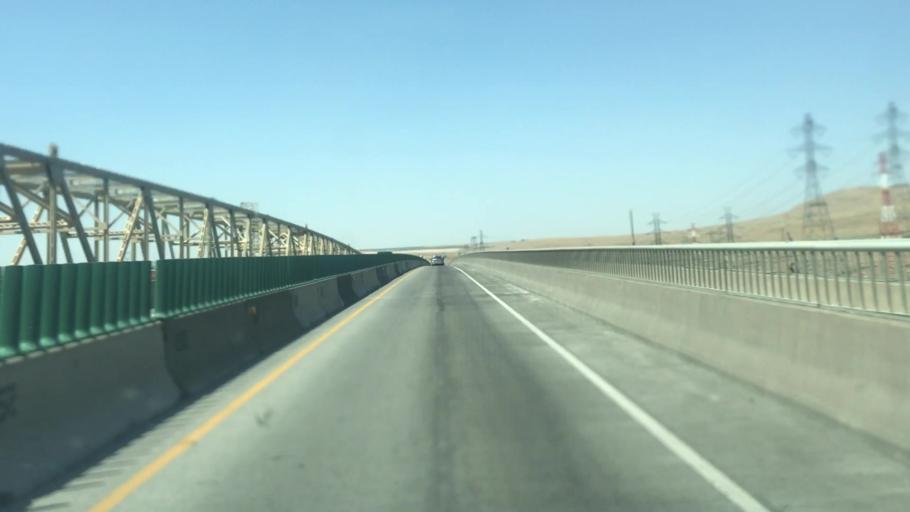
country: US
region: Oregon
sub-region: Umatilla County
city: Umatilla
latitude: 45.9297
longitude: -119.3274
